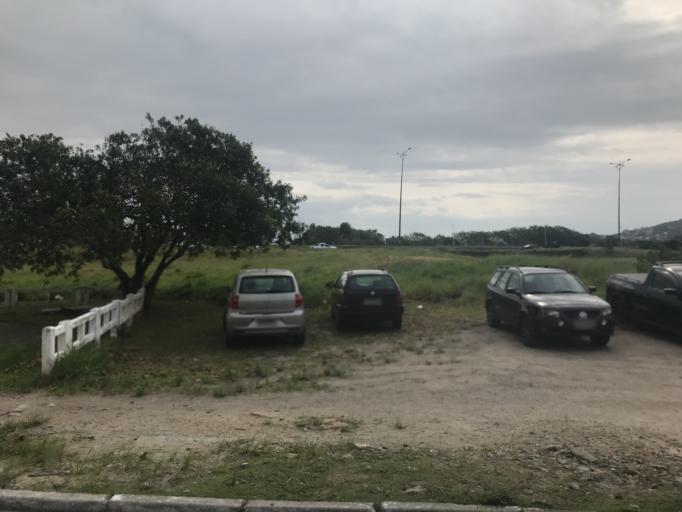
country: BR
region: Santa Catarina
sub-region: Florianopolis
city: Costeira do Pirajubae
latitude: -27.6228
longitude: -48.5267
